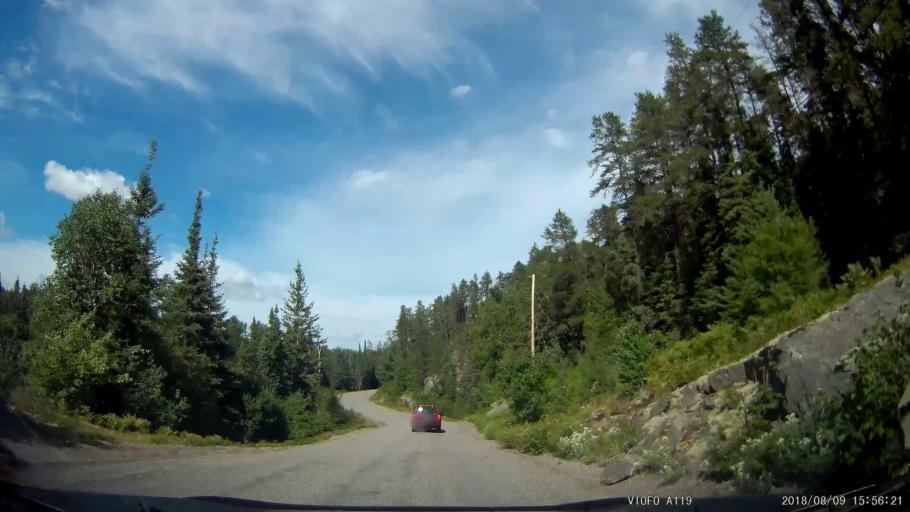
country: CA
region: Ontario
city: Rayside-Balfour
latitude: 46.6060
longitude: -81.5146
